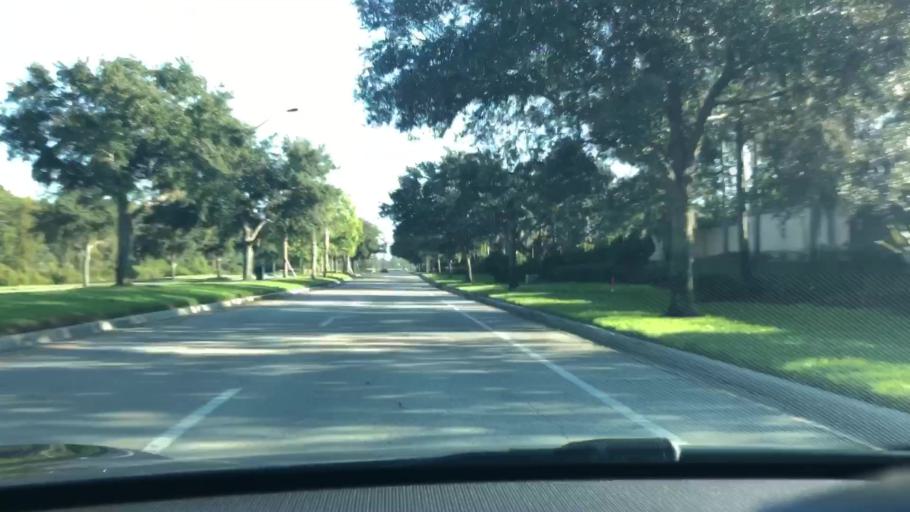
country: US
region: Florida
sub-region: Orange County
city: Meadow Woods
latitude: 28.3942
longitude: -81.2746
